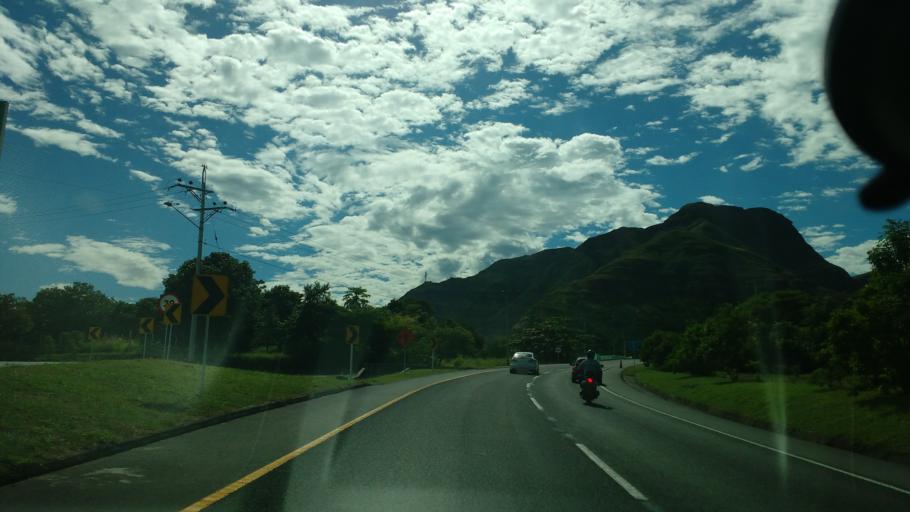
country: CO
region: Tolima
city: Valle de San Juan
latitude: 4.2780
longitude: -75.0130
